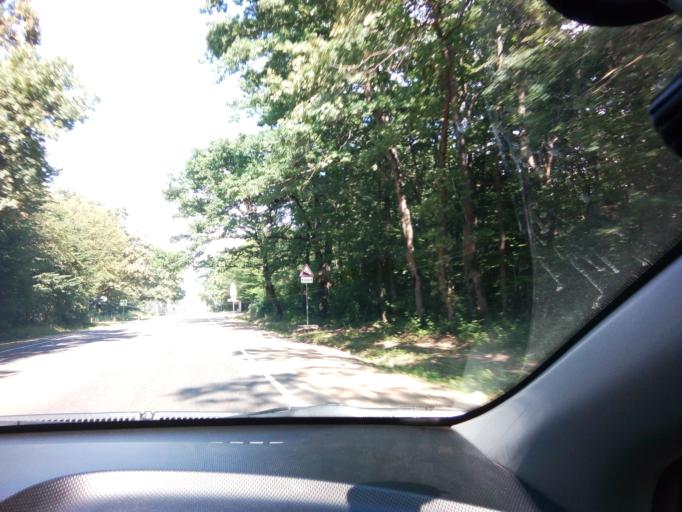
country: RU
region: Krasnodarskiy
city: Apsheronsk
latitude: 44.4615
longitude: 39.6881
